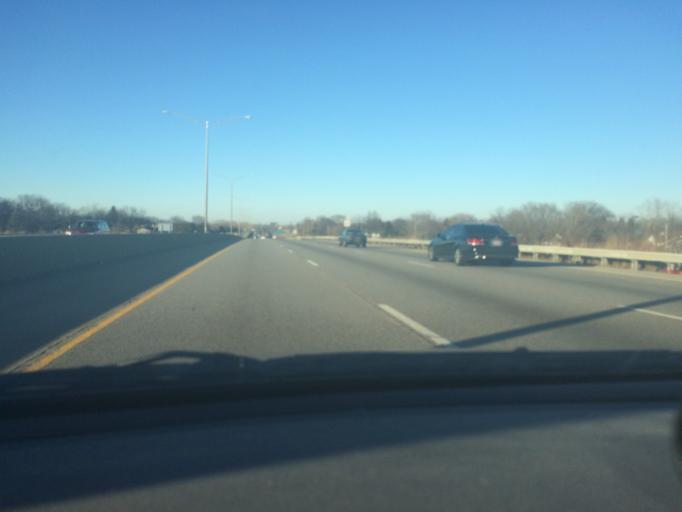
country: US
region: Illinois
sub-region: Cook County
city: Palatine
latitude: 42.1146
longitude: -88.0033
